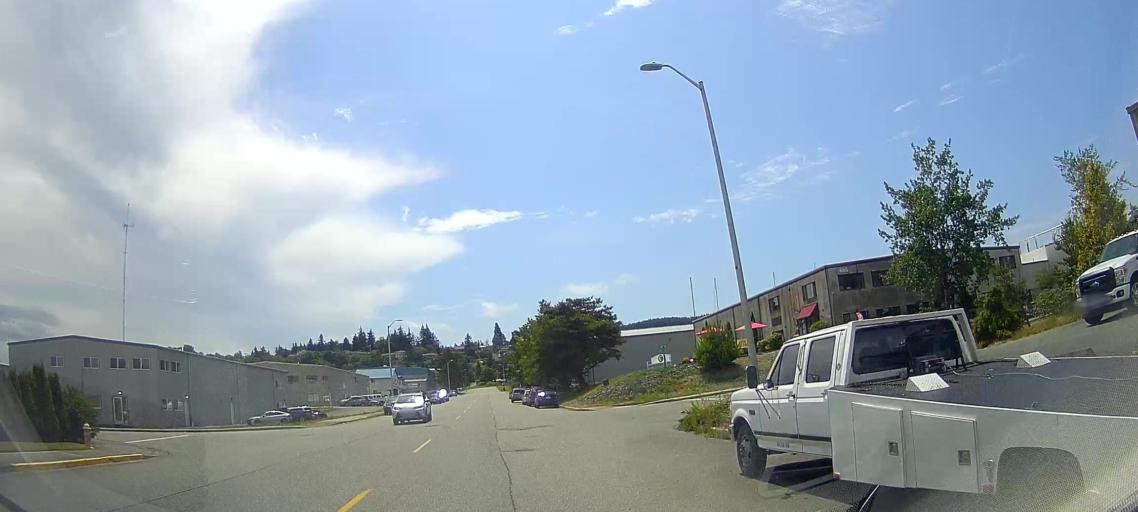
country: US
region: Washington
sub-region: Skagit County
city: Anacortes
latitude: 48.4981
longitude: -122.6067
